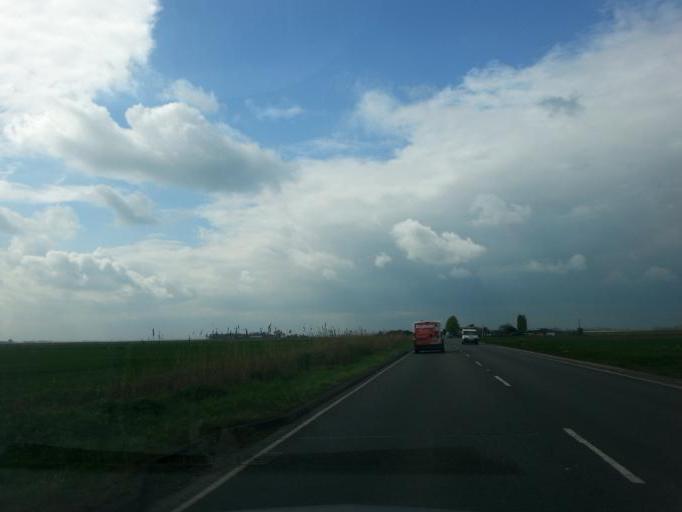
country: GB
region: England
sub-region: Peterborough
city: Thorney
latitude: 52.6153
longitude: -0.0074
